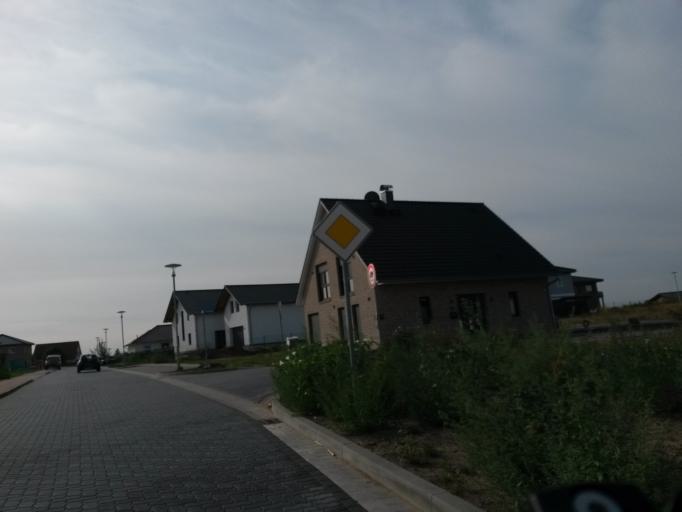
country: DE
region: Saxony-Anhalt
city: Tangermunde
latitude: 52.5410
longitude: 11.9470
